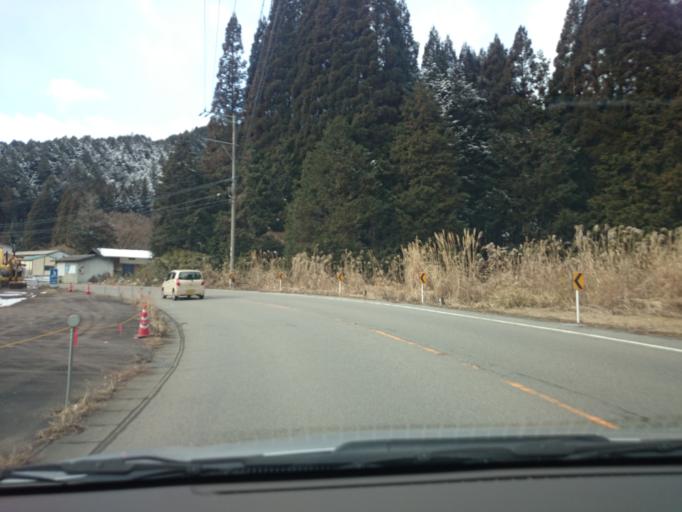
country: JP
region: Gifu
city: Gujo
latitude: 35.7417
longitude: 137.0622
